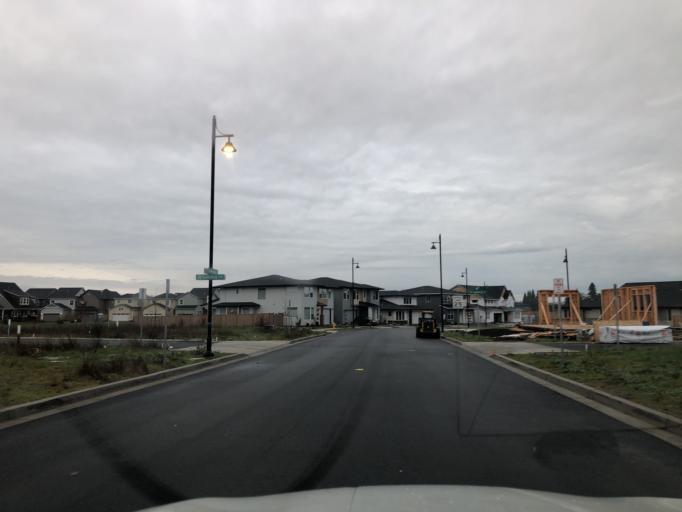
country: US
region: Oregon
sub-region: Washington County
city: Aloha
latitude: 45.4960
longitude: -122.9092
